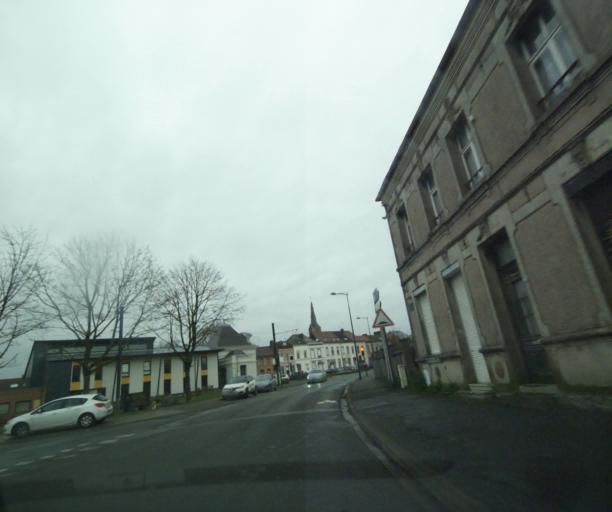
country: FR
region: Nord-Pas-de-Calais
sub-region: Departement du Nord
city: Fresnes-sur-Escaut
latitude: 50.4313
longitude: 3.5790
